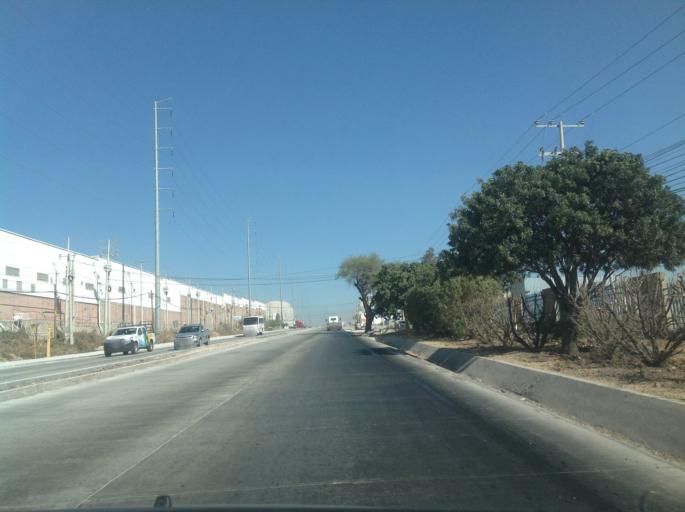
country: MX
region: Queretaro
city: El Colorado
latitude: 20.5586
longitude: -100.2673
